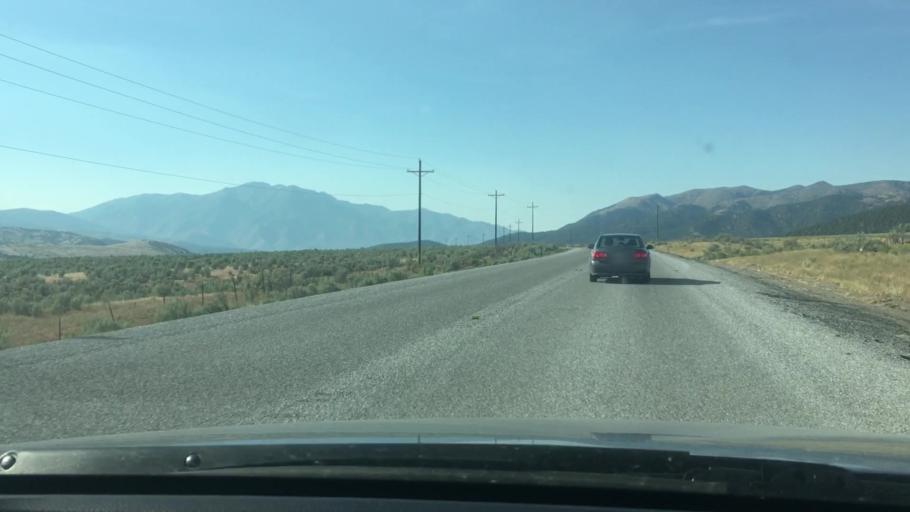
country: US
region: Utah
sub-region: Sanpete County
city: Fairview
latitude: 39.8368
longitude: -111.5124
